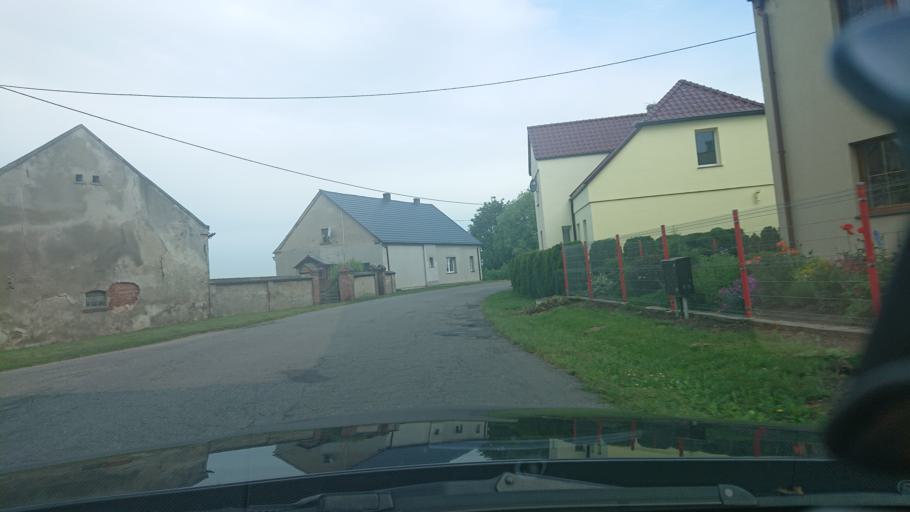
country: PL
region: Greater Poland Voivodeship
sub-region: Powiat gnieznienski
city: Mieleszyn
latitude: 52.6053
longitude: 17.5452
